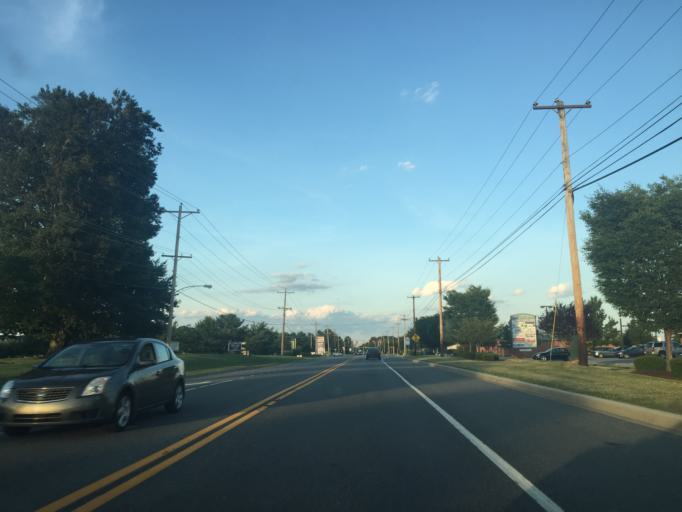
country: US
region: Delaware
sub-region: New Castle County
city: Middletown
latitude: 39.4503
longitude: -75.7047
